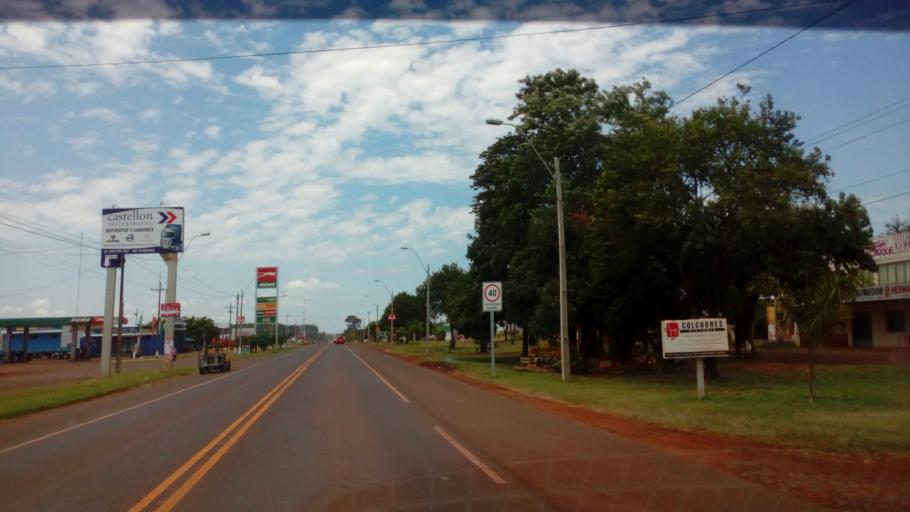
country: PY
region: Alto Parana
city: Santa Rita
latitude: -25.7519
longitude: -55.0572
